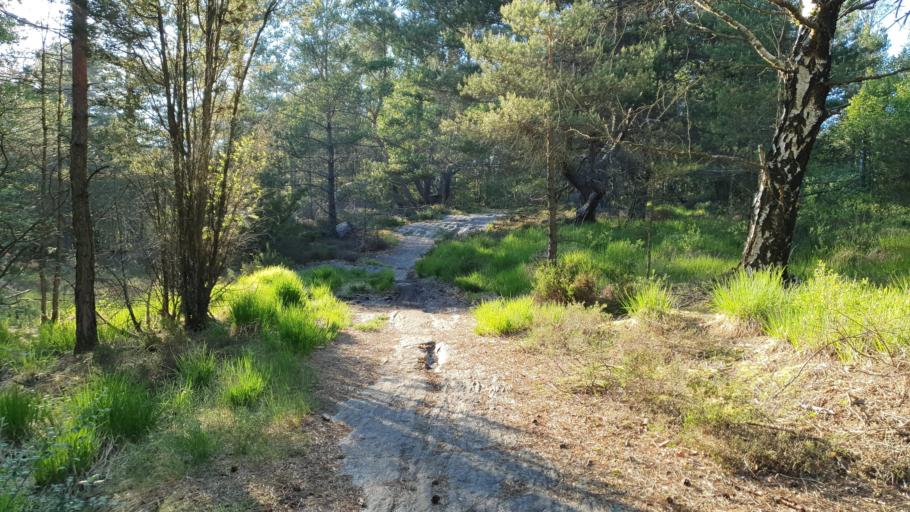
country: SE
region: Vaestra Goetaland
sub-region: Molndal
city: Kallered
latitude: 57.6317
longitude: 12.0603
